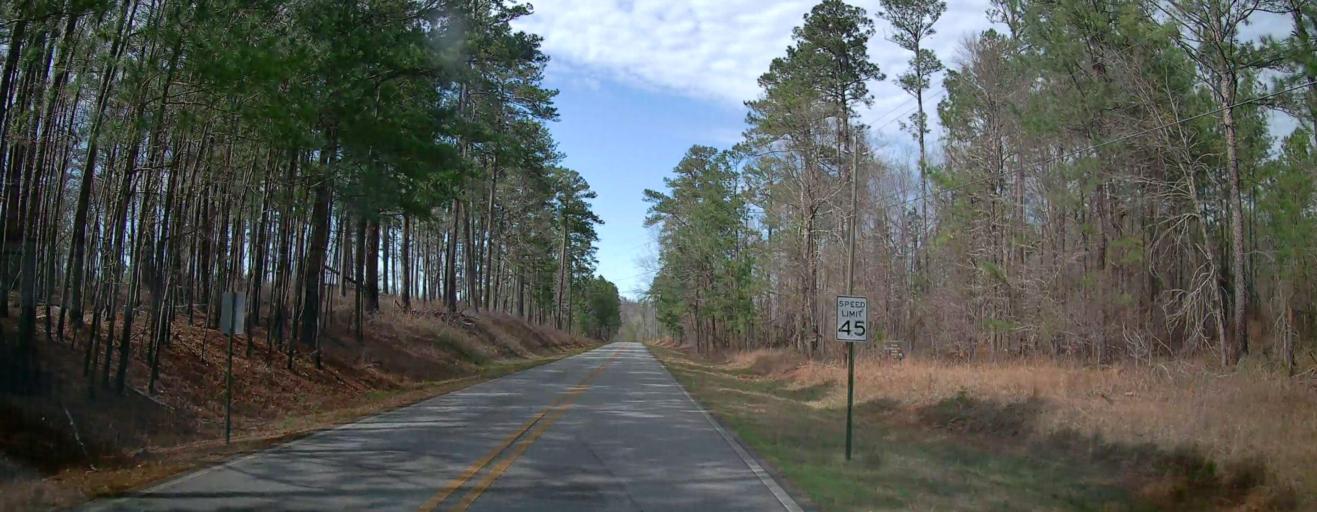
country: US
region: Georgia
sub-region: Jones County
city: Gray
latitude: 33.0266
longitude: -83.7028
